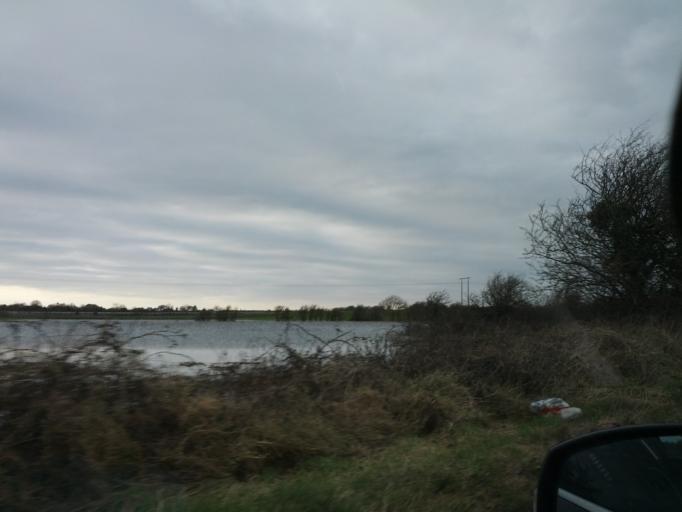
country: IE
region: Connaught
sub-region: County Galway
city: Gort
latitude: 53.1564
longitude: -8.8502
